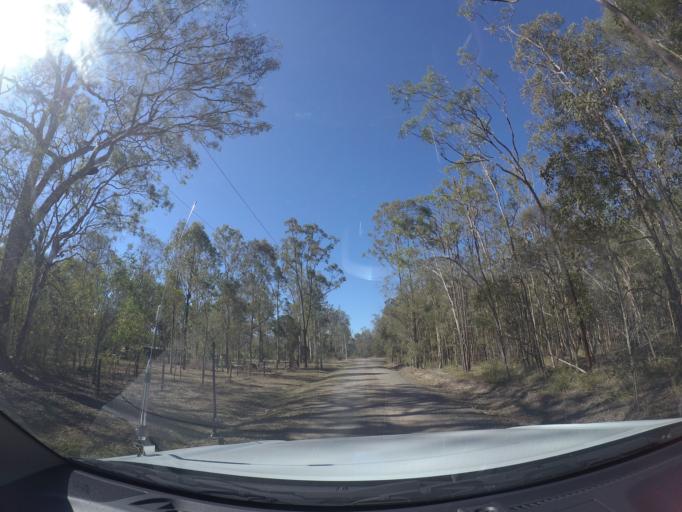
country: AU
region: Queensland
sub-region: Logan
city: Park Ridge South
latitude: -27.7463
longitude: 153.0507
